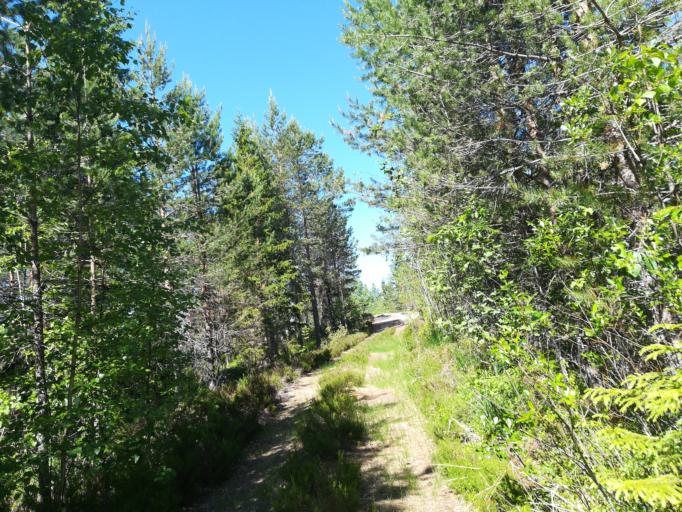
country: FI
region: Southern Savonia
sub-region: Mikkeli
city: Puumala
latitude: 61.6179
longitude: 28.1620
